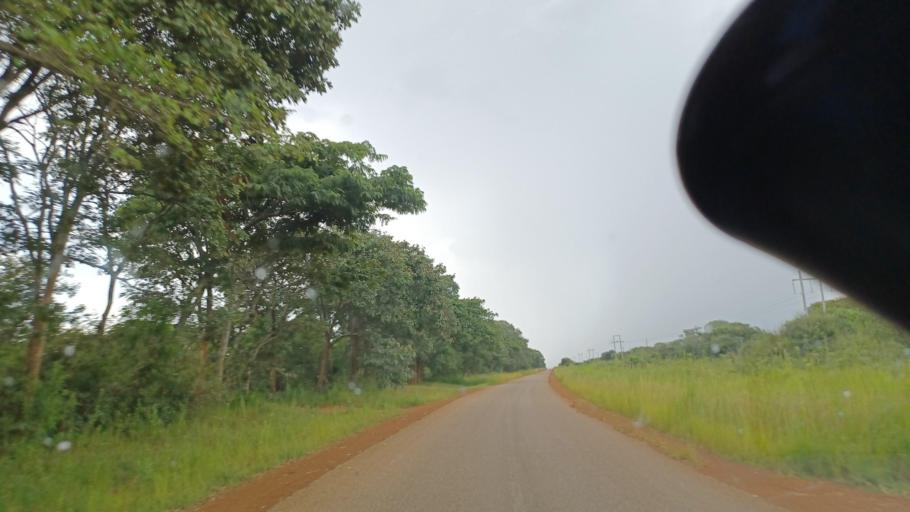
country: ZM
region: North-Western
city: Kasempa
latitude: -13.0464
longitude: 25.9913
